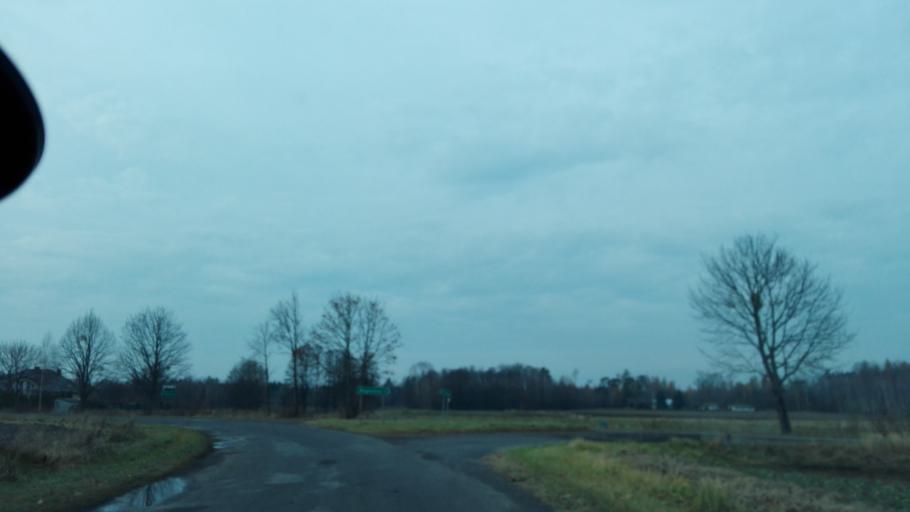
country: PL
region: Lublin Voivodeship
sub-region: Powiat bialski
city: Sosnowka
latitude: 51.7423
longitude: 23.3918
